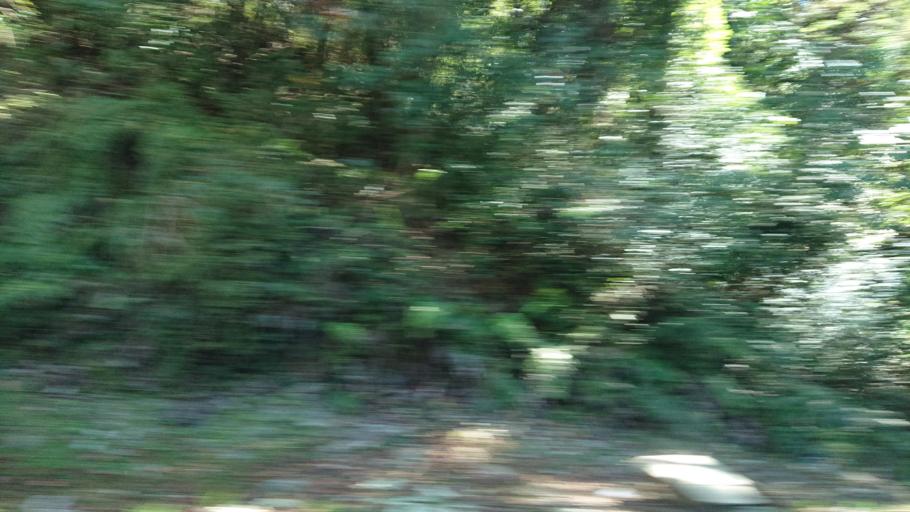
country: TW
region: Taiwan
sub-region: Hualien
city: Hualian
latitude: 24.3723
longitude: 121.3399
